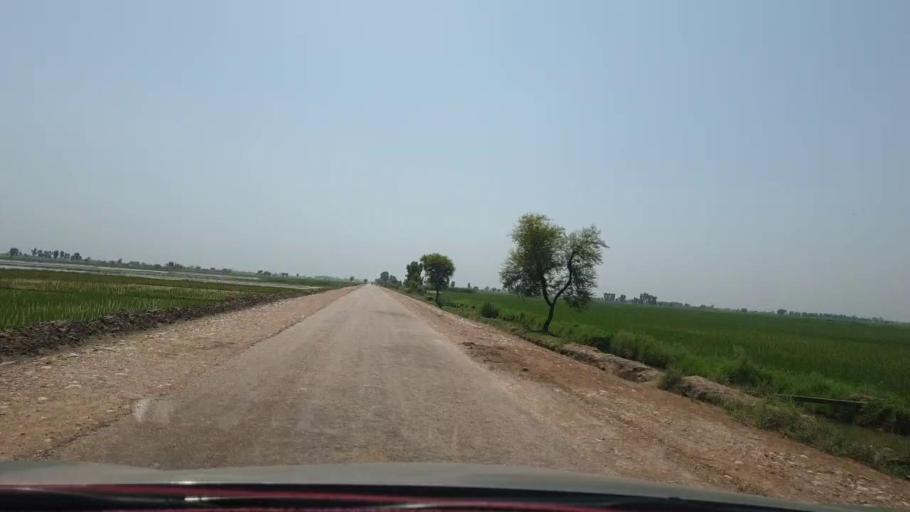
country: PK
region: Sindh
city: Warah
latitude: 27.5659
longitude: 67.8024
